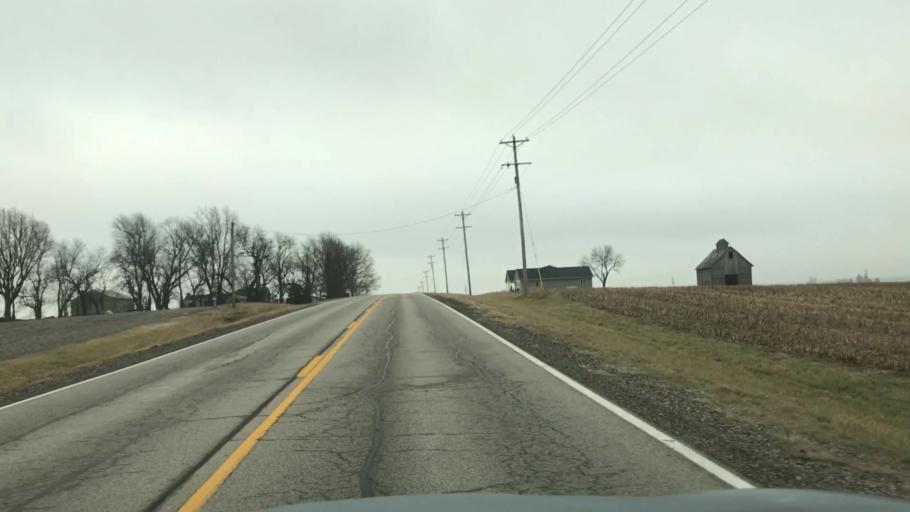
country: US
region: Illinois
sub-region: McLean County
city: Hudson
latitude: 40.5718
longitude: -88.9447
